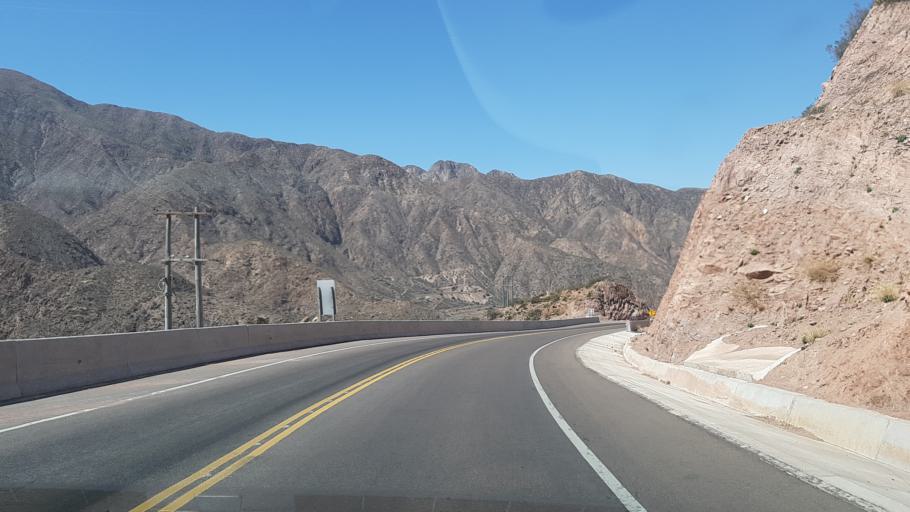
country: AR
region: Mendoza
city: Lujan de Cuyo
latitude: -32.9998
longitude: -69.1331
